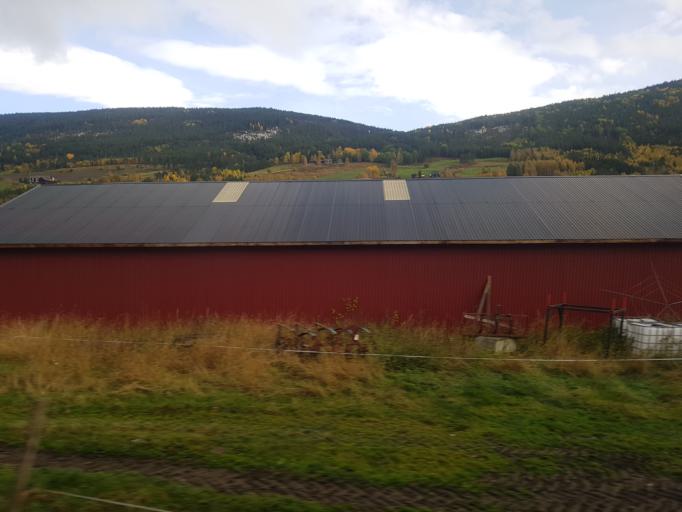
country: NO
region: Oppland
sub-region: Dovre
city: Dovre
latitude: 61.9751
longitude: 9.2569
